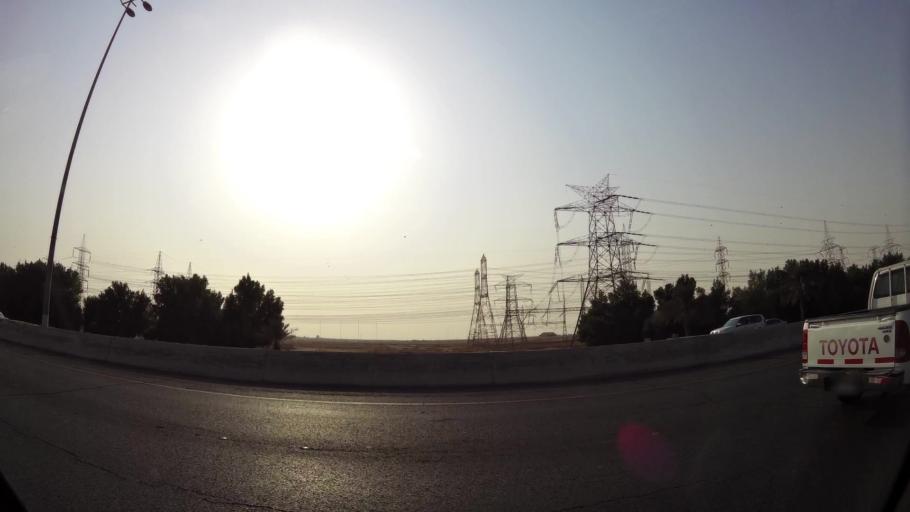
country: KW
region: Mubarak al Kabir
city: Sabah as Salim
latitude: 29.2190
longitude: 48.0562
